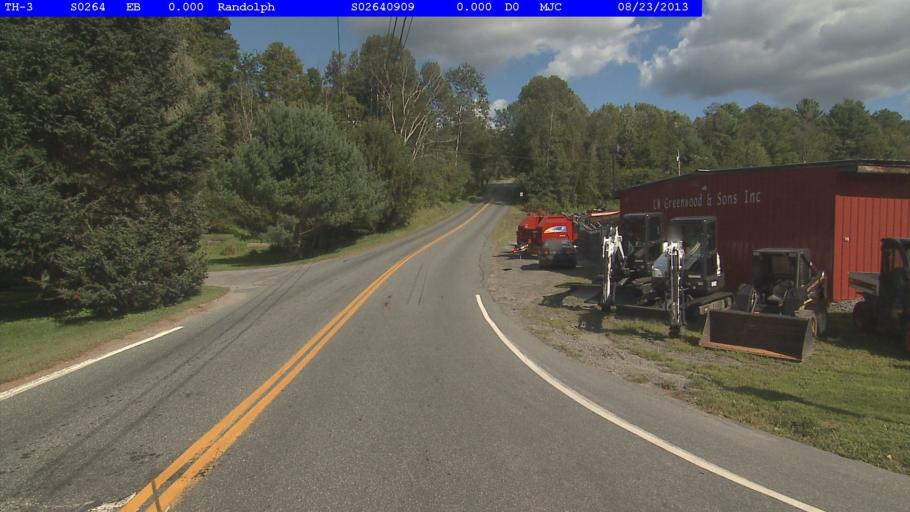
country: US
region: Vermont
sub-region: Orange County
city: Randolph
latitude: 43.9366
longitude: -72.5526
